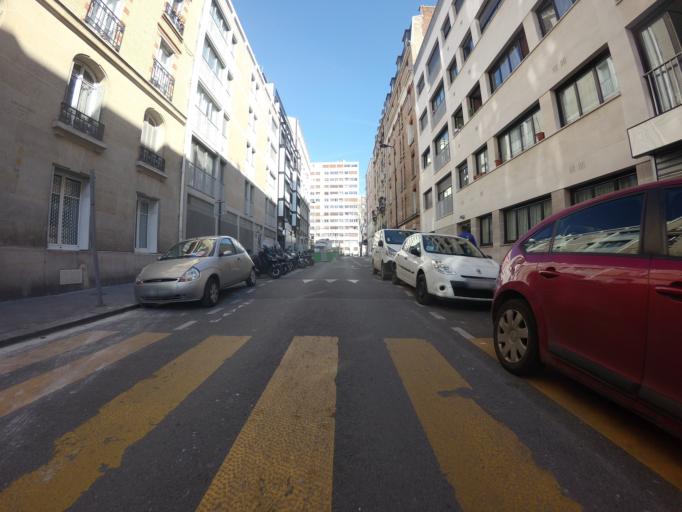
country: FR
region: Ile-de-France
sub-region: Paris
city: Saint-Ouen
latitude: 48.8953
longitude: 2.3233
